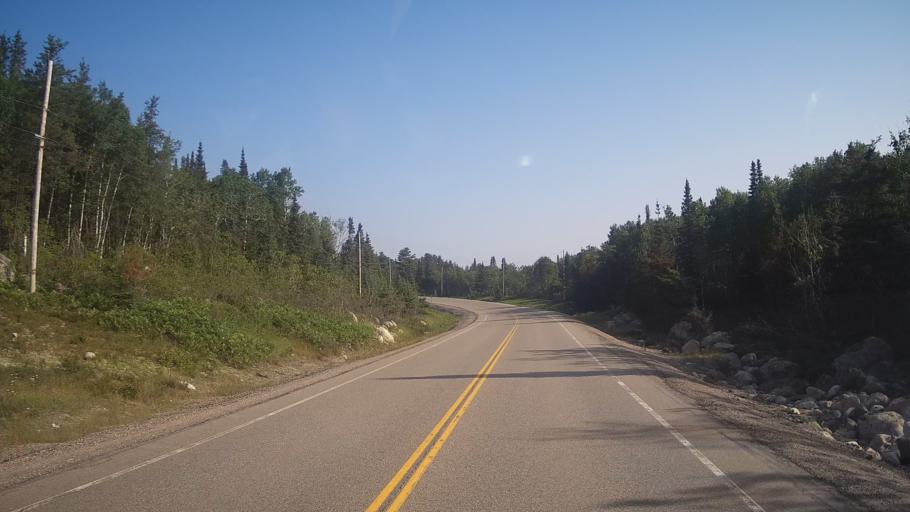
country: CA
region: Ontario
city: Rayside-Balfour
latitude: 46.7107
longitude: -81.5617
